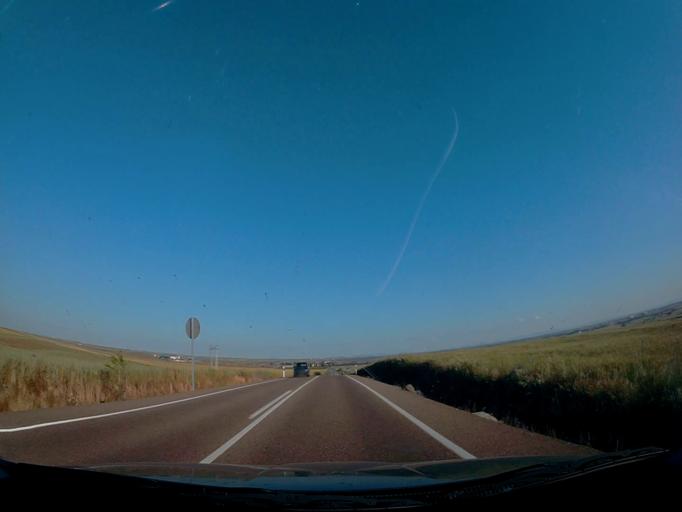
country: ES
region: Castille-La Mancha
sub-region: Province of Toledo
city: Maqueda
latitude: 40.0849
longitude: -4.3836
